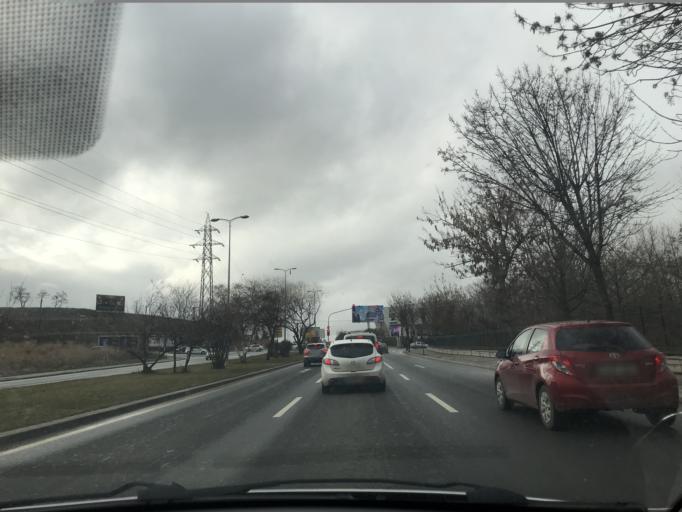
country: TR
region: Ankara
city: Batikent
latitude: 39.9597
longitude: 32.7829
